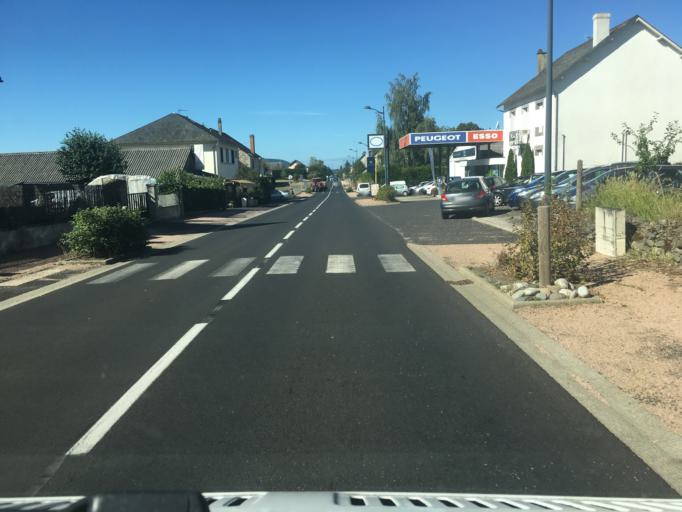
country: FR
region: Auvergne
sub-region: Departement du Cantal
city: Lanobre
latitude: 45.4426
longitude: 2.5354
